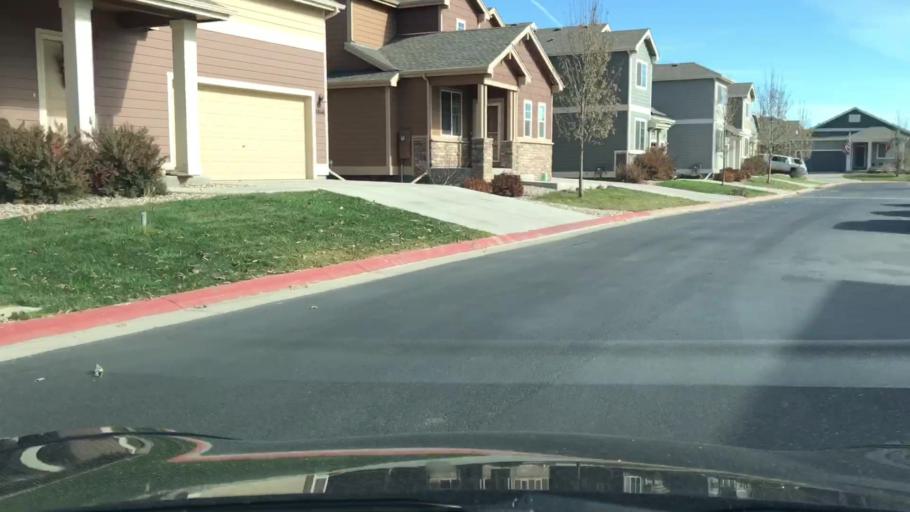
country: US
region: Colorado
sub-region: Larimer County
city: Fort Collins
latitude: 40.5944
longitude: -105.0435
